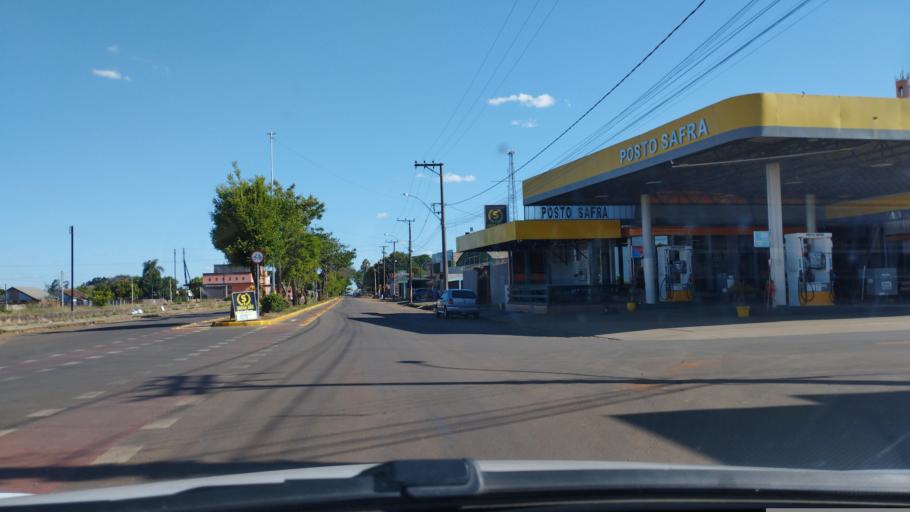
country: BR
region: Rio Grande do Sul
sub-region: Tupancireta
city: Tupancireta
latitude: -29.0796
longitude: -53.8358
